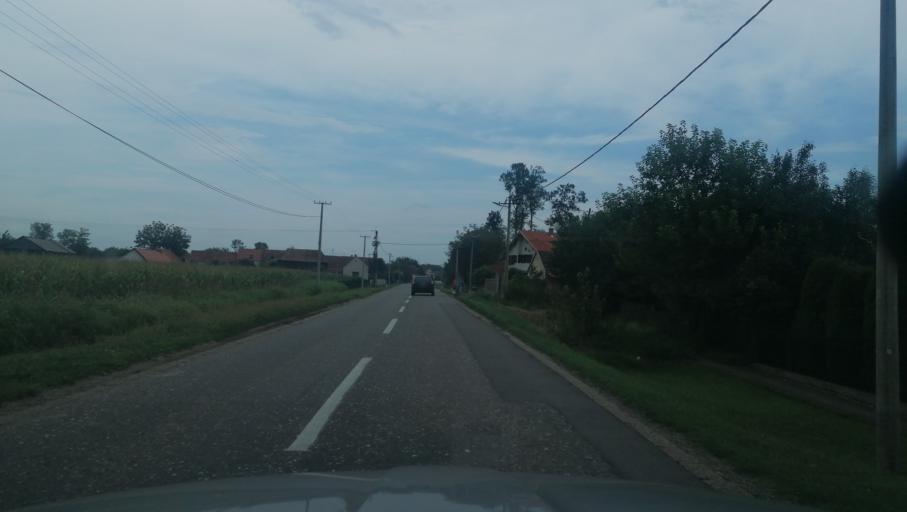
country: RS
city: Klenje
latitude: 44.8124
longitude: 19.4416
